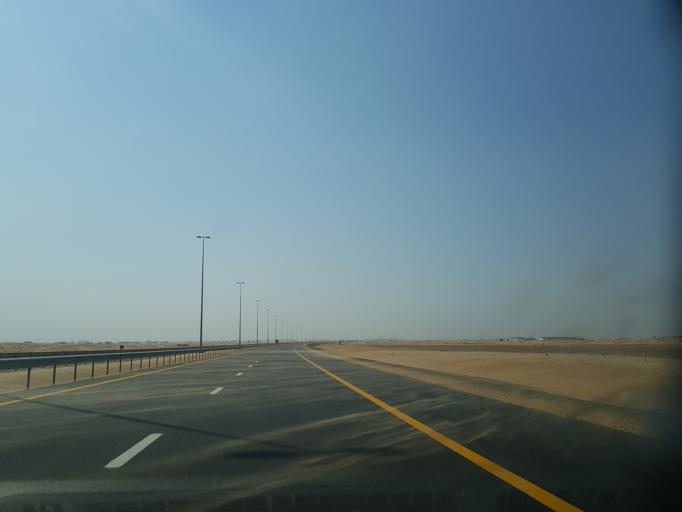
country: AE
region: Ash Shariqah
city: Sharjah
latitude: 25.2713
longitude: 55.6344
